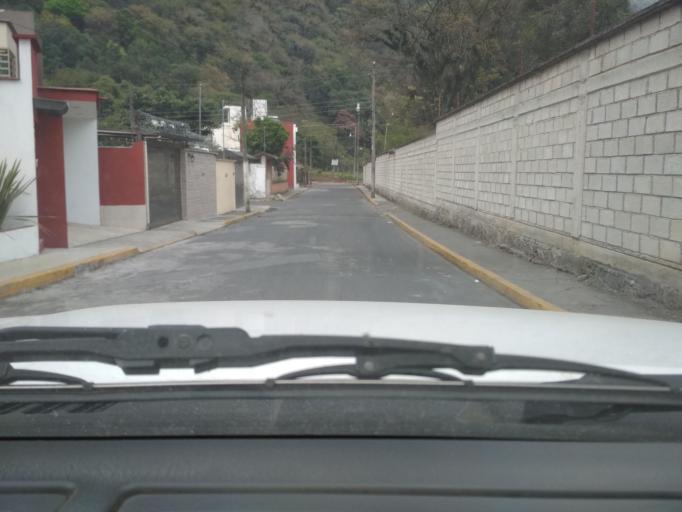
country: MX
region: Veracruz
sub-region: Mariano Escobedo
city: Palmira
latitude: 18.8738
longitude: -97.0990
